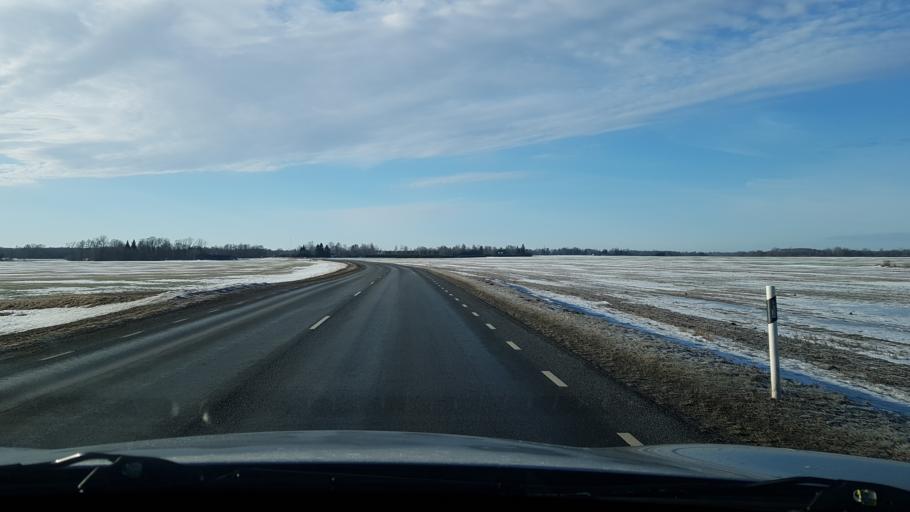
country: EE
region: Viljandimaa
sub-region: Vohma linn
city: Vohma
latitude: 58.6481
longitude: 25.5846
